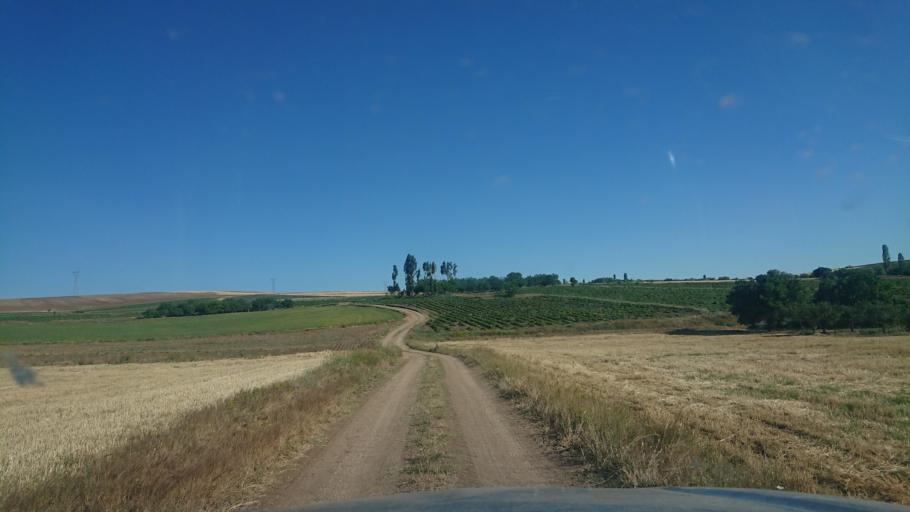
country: TR
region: Aksaray
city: Agacoren
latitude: 38.8296
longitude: 33.9527
